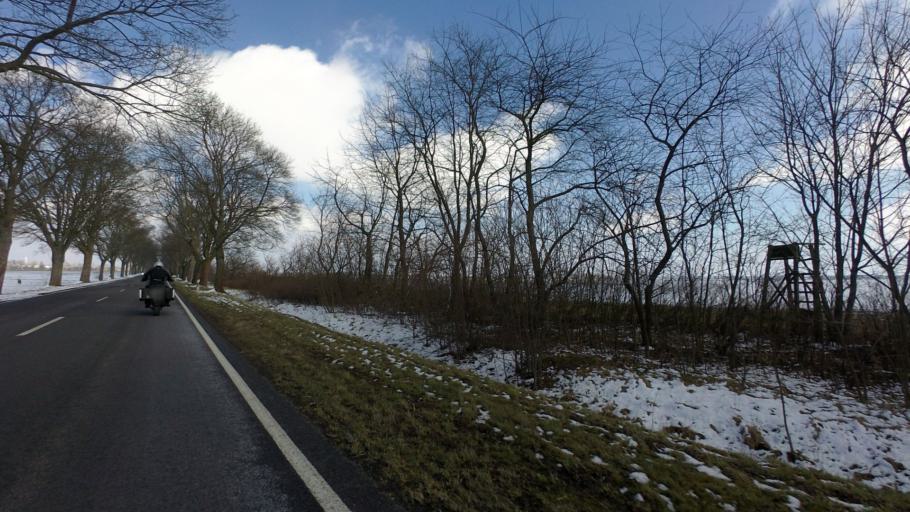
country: DE
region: Brandenburg
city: Werftpfuhl
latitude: 52.7260
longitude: 13.8377
